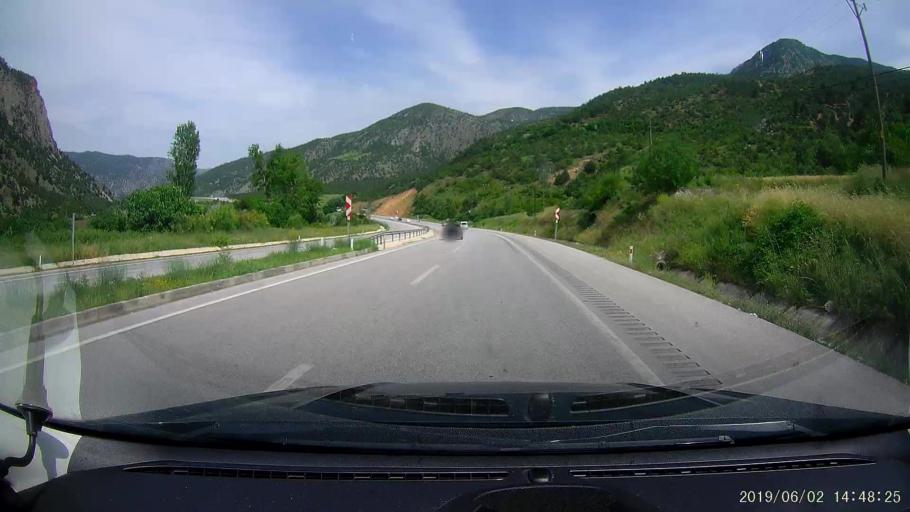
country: TR
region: Corum
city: Hacihamza
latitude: 41.0628
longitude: 34.4800
